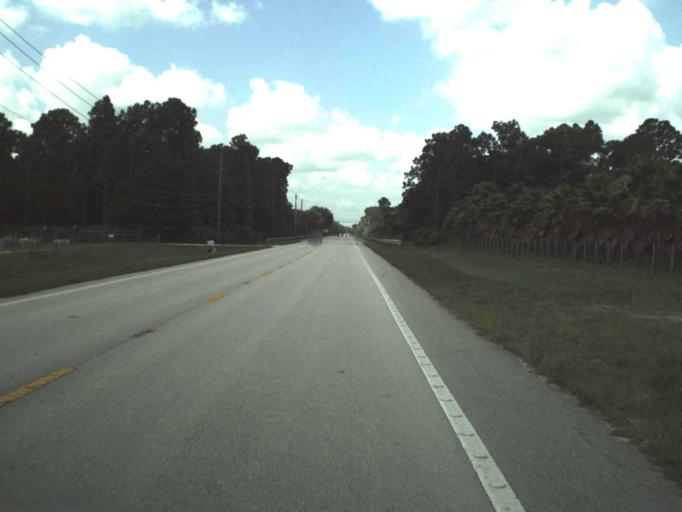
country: US
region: Florida
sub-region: Volusia County
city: Samsula-Spruce Creek
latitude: 28.9447
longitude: -81.1014
